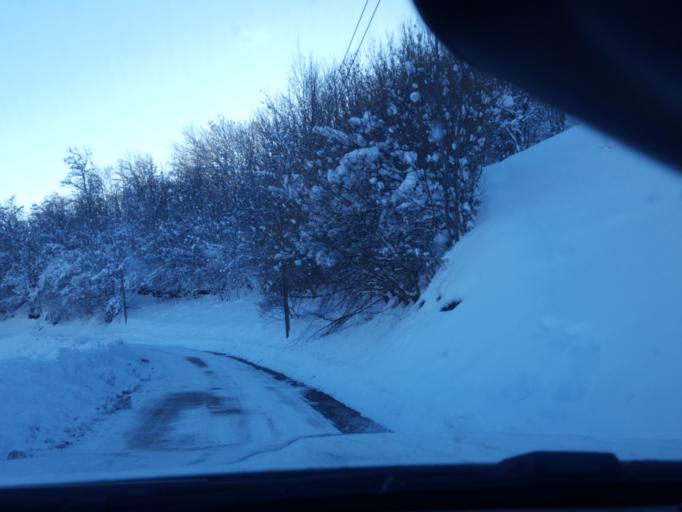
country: FR
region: Rhone-Alpes
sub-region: Departement de la Savoie
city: Salins-les-Thermes
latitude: 45.4621
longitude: 6.5102
